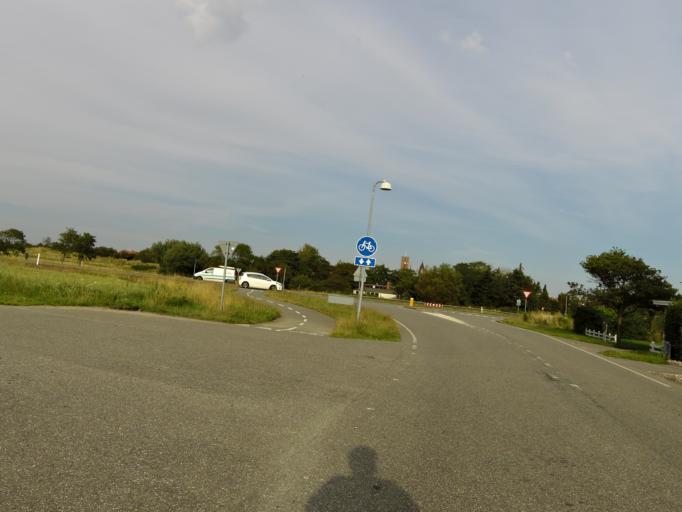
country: DK
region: South Denmark
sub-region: Esbjerg Kommune
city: Ribe
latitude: 55.3277
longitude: 8.7517
